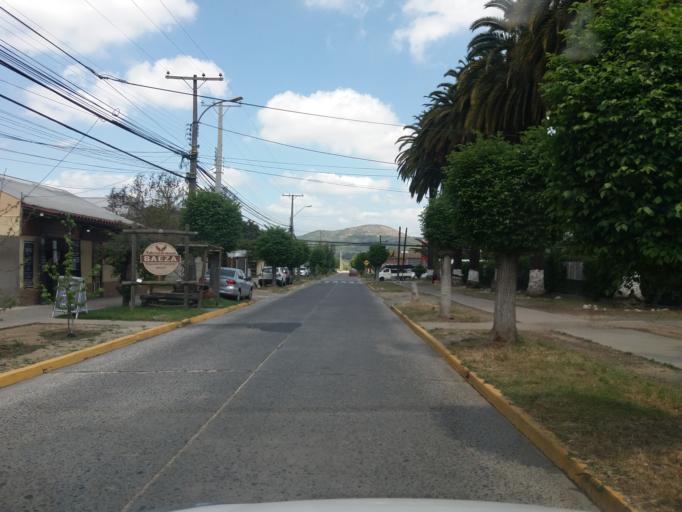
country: CL
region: Valparaiso
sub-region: Provincia de Marga Marga
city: Limache
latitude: -32.9864
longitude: -71.2781
